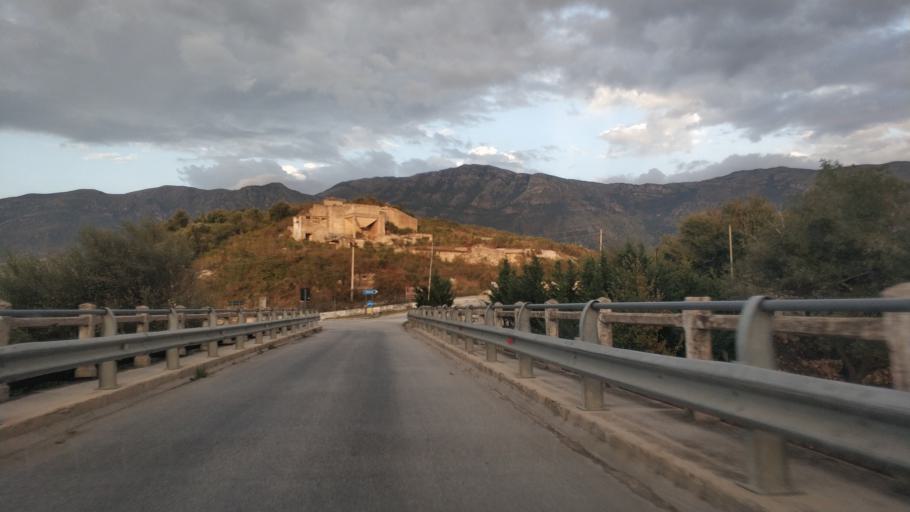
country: AL
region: Vlore
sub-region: Rrethi i Vlores
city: Orikum
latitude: 40.3317
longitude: 19.4770
